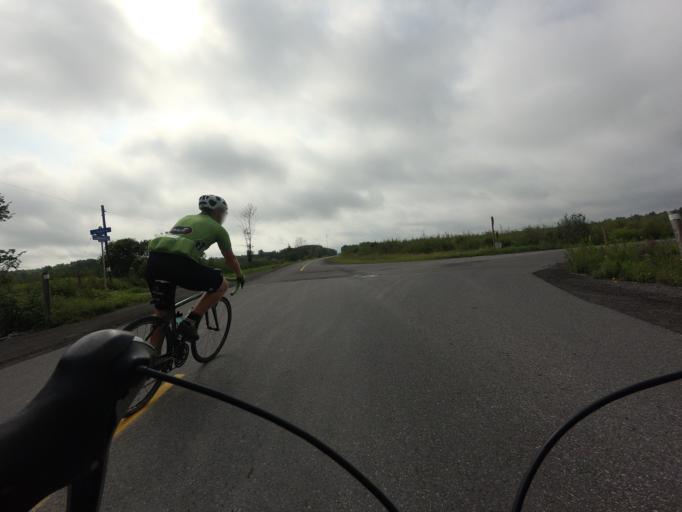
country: CA
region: Ontario
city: Bells Corners
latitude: 45.0573
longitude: -75.7147
